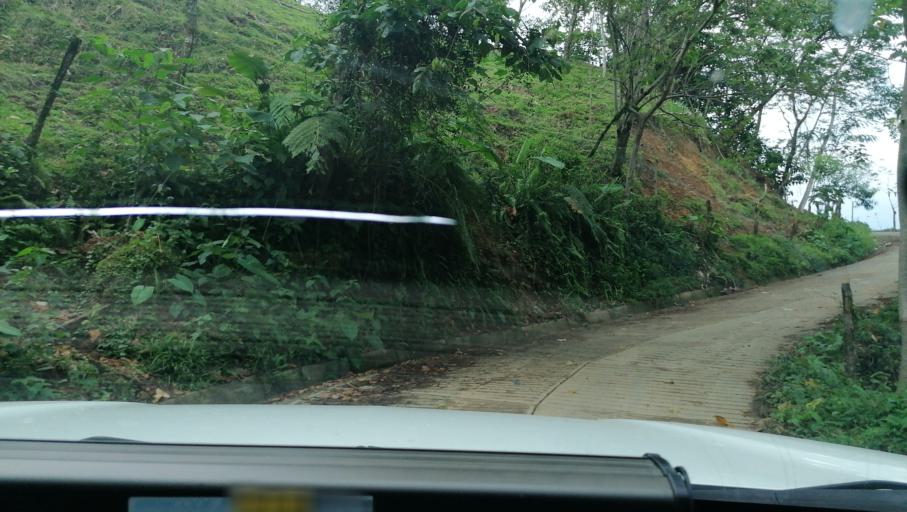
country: MX
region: Chiapas
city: Ixtacomitan
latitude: 17.3337
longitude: -93.1073
